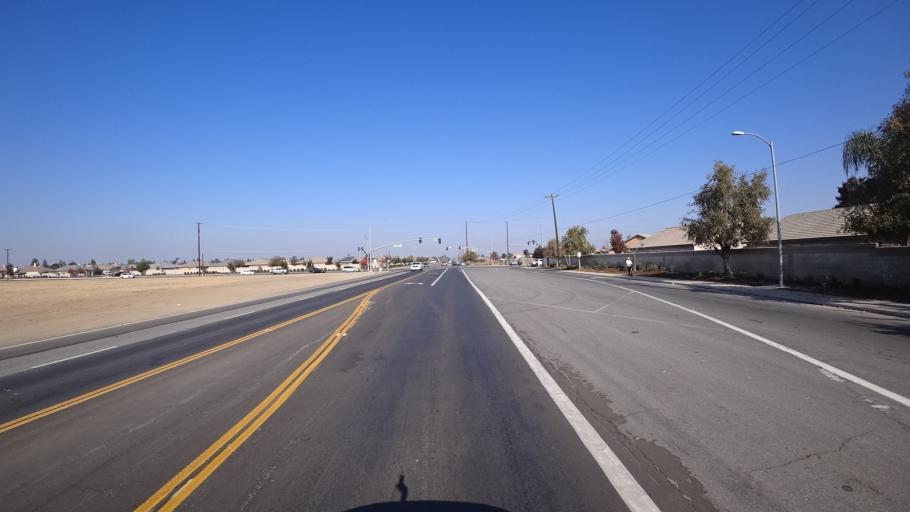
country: US
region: California
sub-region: Kern County
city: Greenfield
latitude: 35.2805
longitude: -119.0390
